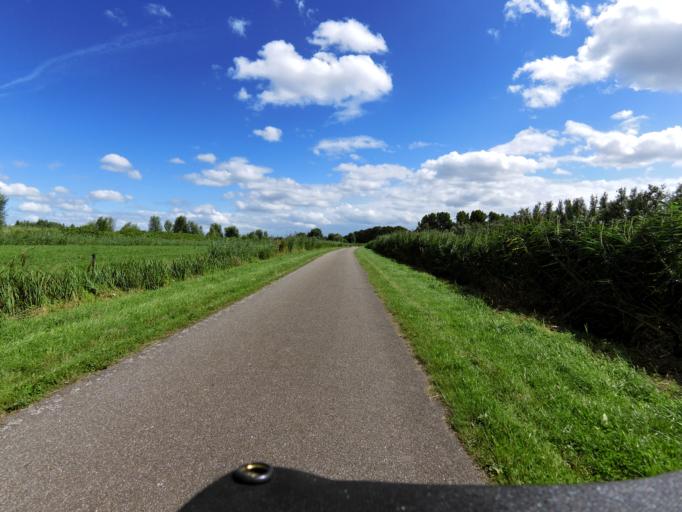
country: NL
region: South Holland
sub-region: Gemeente Zwijndrecht
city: Heerjansdam
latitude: 51.8147
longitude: 4.5706
